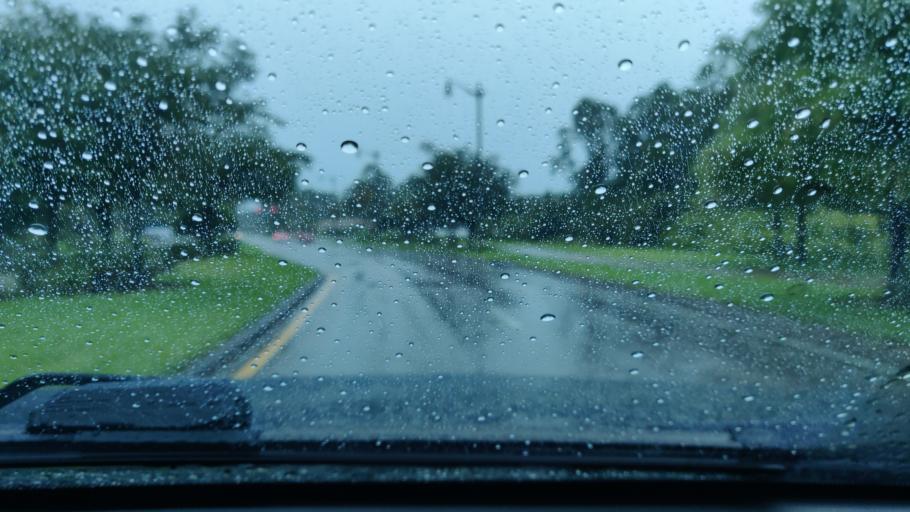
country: US
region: Florida
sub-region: Flagler County
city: Bunnell
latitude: 29.4899
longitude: -81.2197
